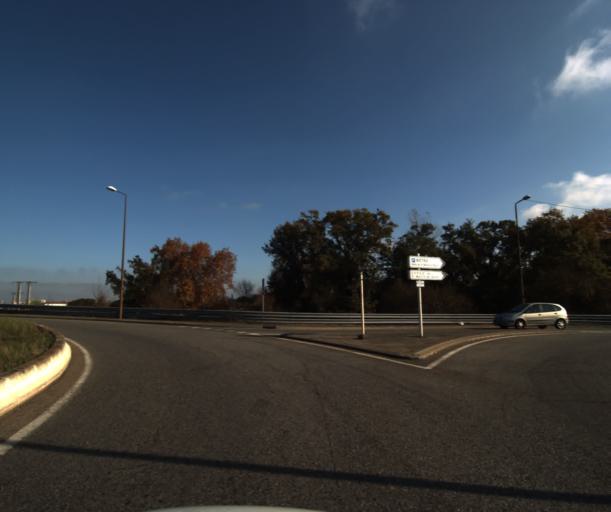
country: FR
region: Midi-Pyrenees
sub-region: Departement de la Haute-Garonne
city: Colomiers
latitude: 43.5970
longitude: 1.3640
